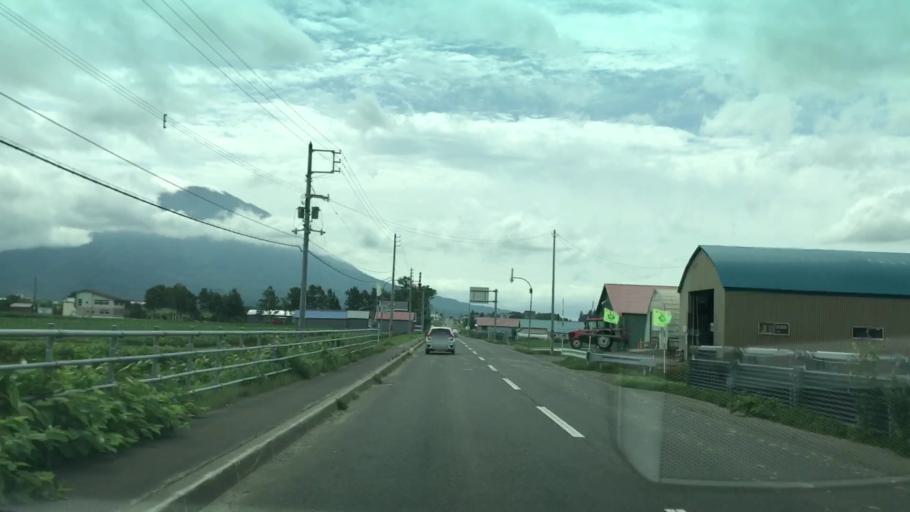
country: JP
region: Hokkaido
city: Niseko Town
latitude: 42.9316
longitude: 140.7759
